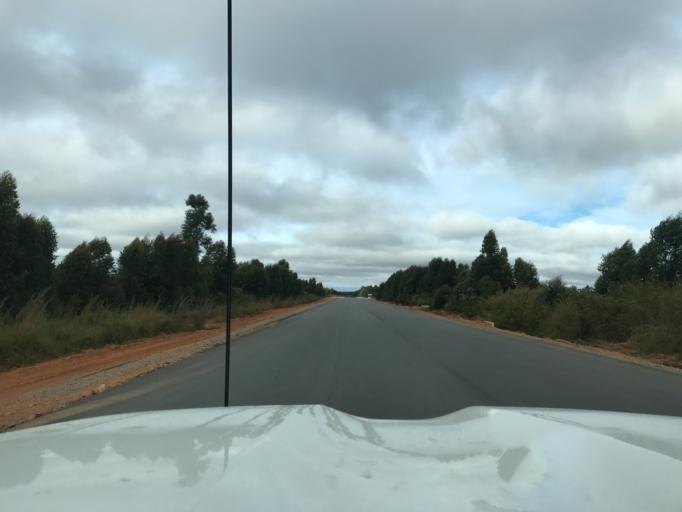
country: TZ
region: Iringa
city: Makungu
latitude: -8.3702
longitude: 35.2272
